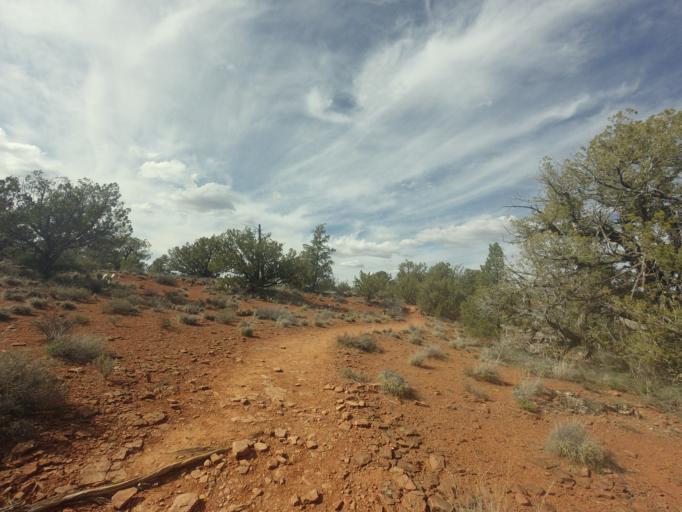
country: US
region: Arizona
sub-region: Yavapai County
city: West Sedona
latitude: 34.8065
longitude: -111.8321
